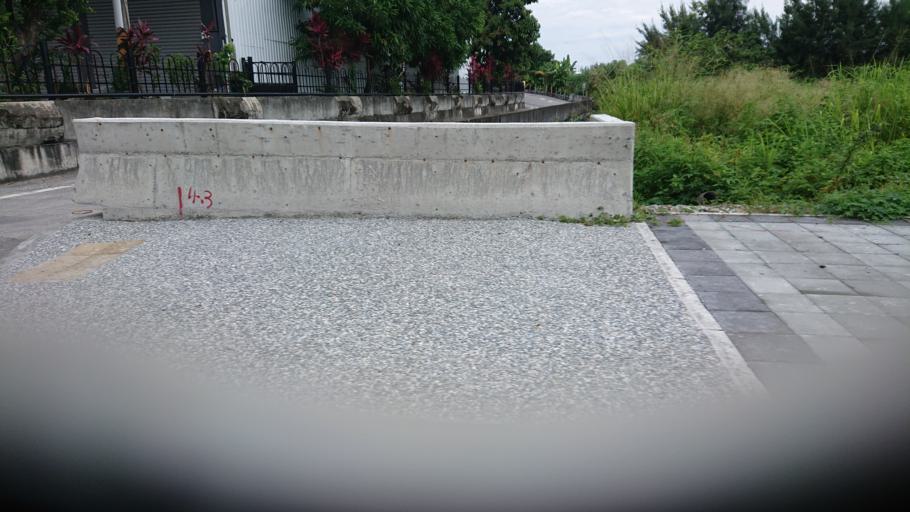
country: TW
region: Taiwan
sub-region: Hualien
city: Hualian
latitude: 23.9613
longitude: 121.6043
